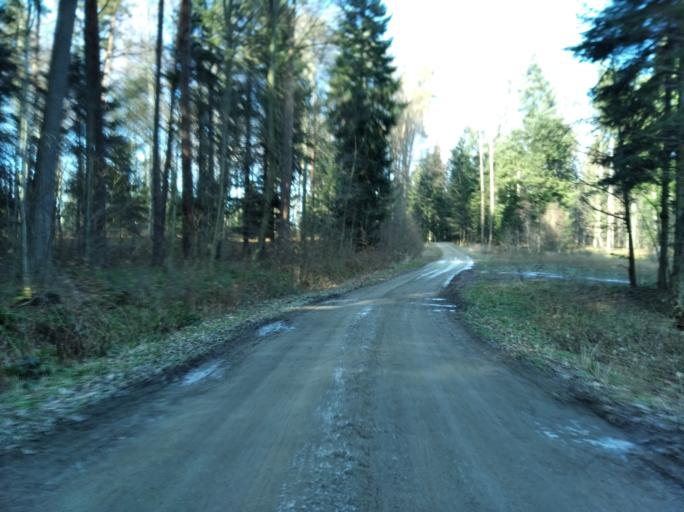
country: PL
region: Subcarpathian Voivodeship
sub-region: Powiat strzyzowski
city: Jawornik
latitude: 49.8330
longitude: 21.8585
